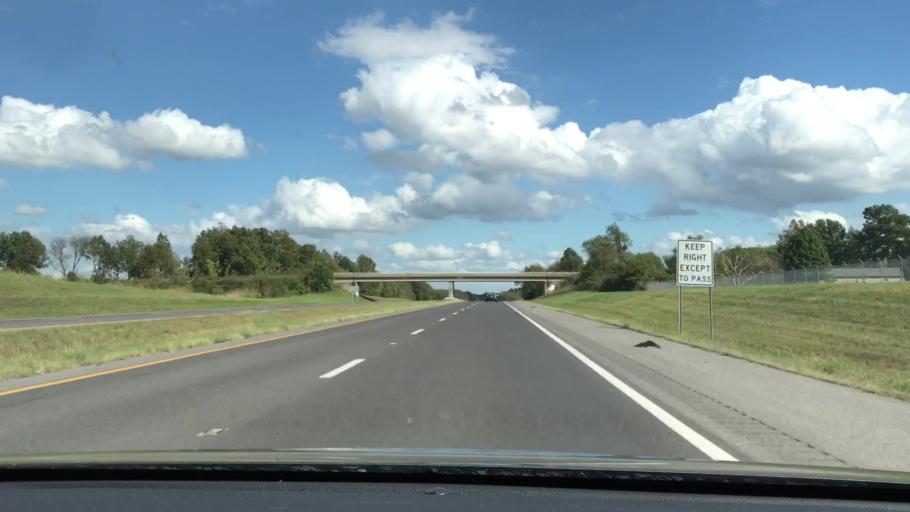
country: US
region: Kentucky
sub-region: Graves County
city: Mayfield
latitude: 36.7776
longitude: -88.5846
